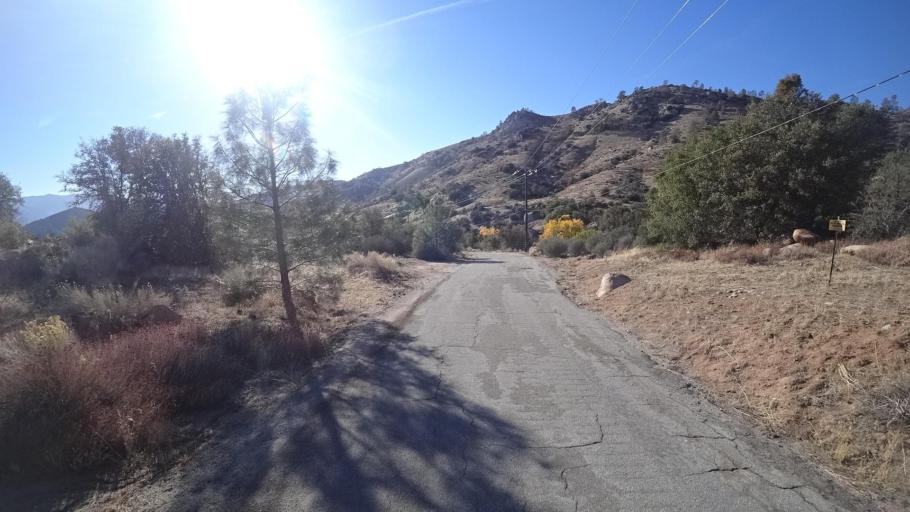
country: US
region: California
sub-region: Kern County
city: Weldon
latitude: 35.7227
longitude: -118.3050
